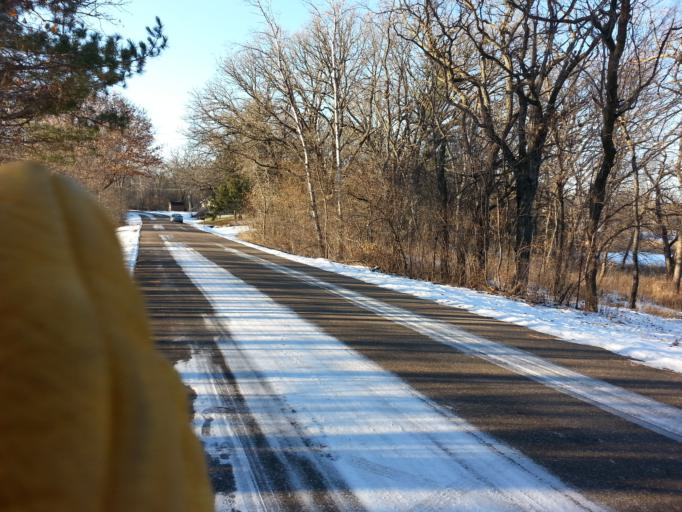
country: US
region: Minnesota
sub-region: Washington County
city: Lakeland
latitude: 44.9641
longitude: -92.8254
